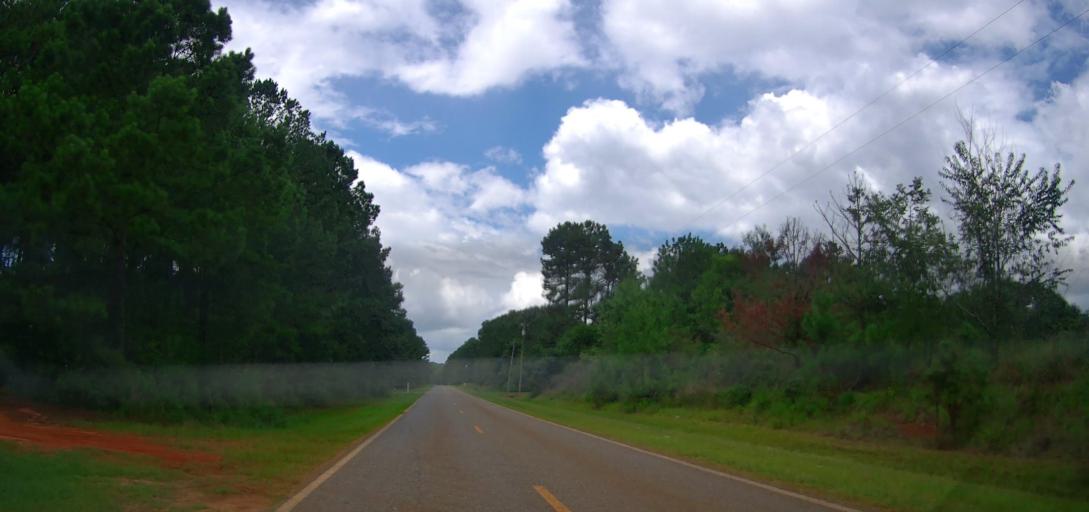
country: US
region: Georgia
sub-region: Pulaski County
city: Hawkinsville
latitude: 32.3450
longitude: -83.5607
